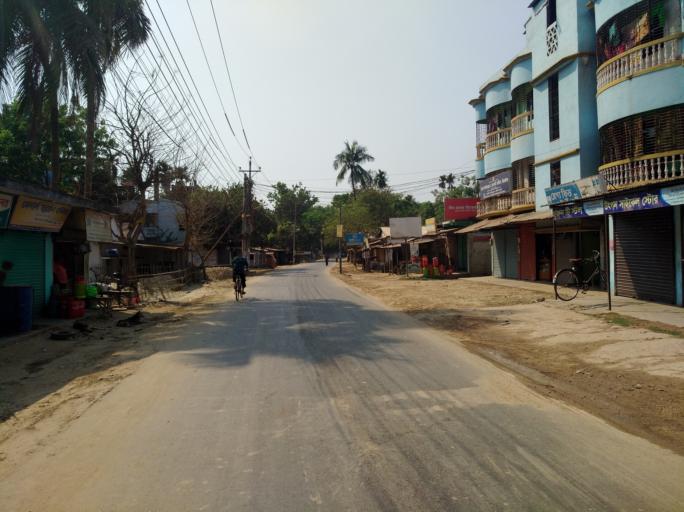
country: BD
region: Khulna
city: Kaliganj
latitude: 23.5503
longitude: 89.1656
